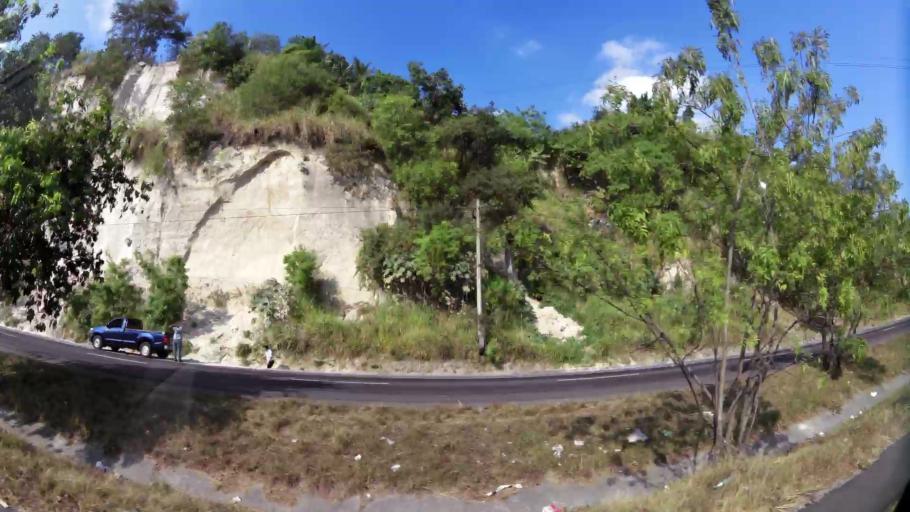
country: SV
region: San Salvador
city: Soyapango
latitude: 13.7114
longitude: -89.1233
